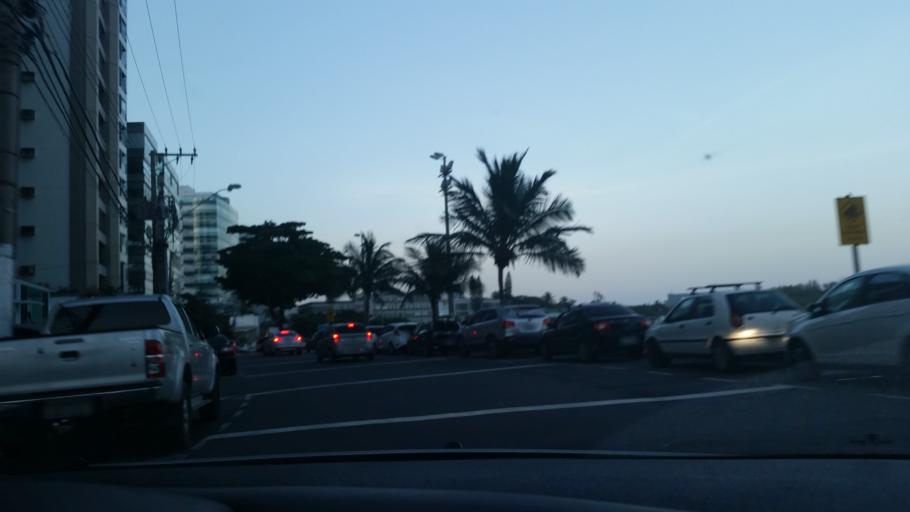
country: BR
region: Espirito Santo
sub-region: Vila Velha
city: Vila Velha
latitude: -20.3313
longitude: -40.2740
